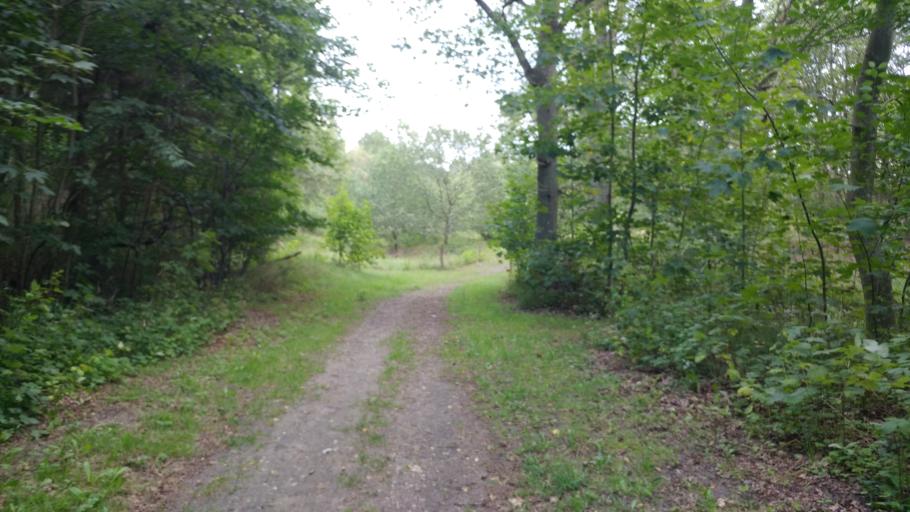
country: DK
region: Central Jutland
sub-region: Norddjurs Kommune
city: Allingabro
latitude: 56.5484
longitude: 10.3699
